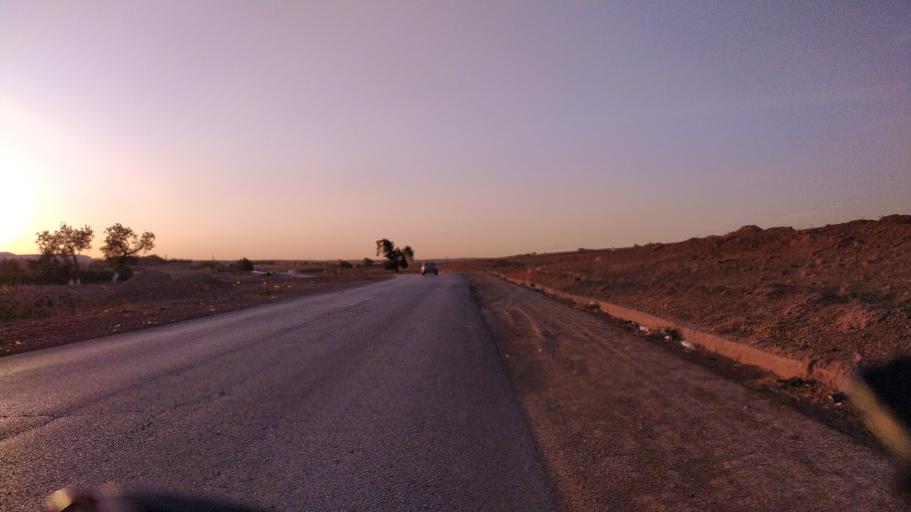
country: DZ
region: Tiaret
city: Frenda
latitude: 34.9010
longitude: 1.2432
